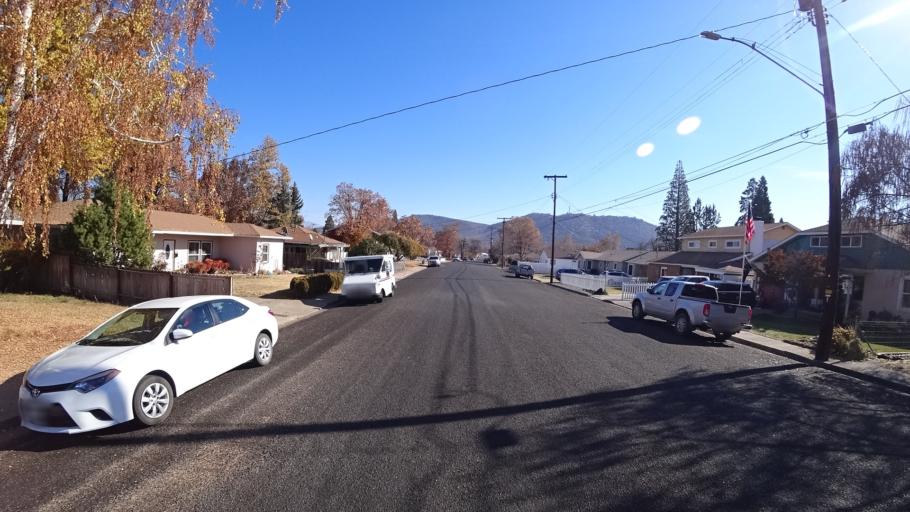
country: US
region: California
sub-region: Siskiyou County
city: Yreka
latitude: 41.7299
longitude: -122.6455
